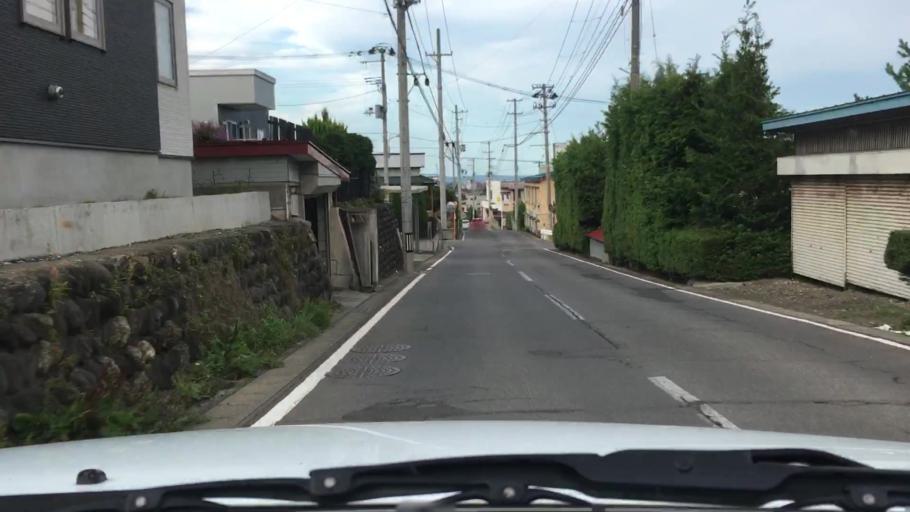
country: JP
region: Aomori
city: Hirosaki
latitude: 40.5800
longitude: 140.4575
